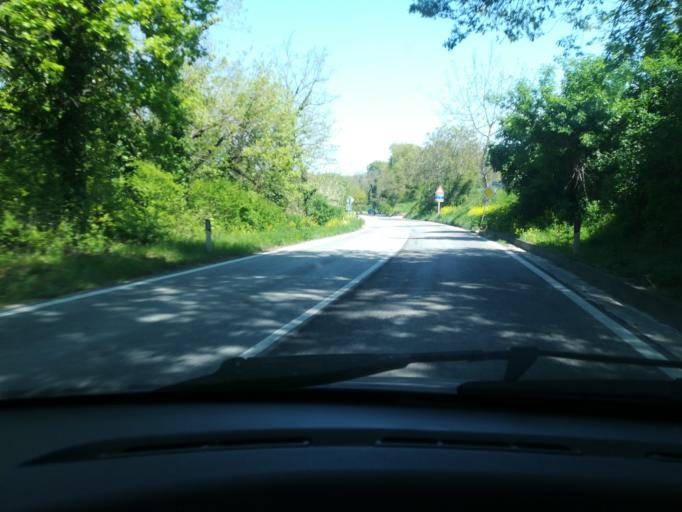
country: IT
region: The Marches
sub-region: Provincia di Macerata
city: Strada
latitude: 43.4060
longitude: 13.2073
